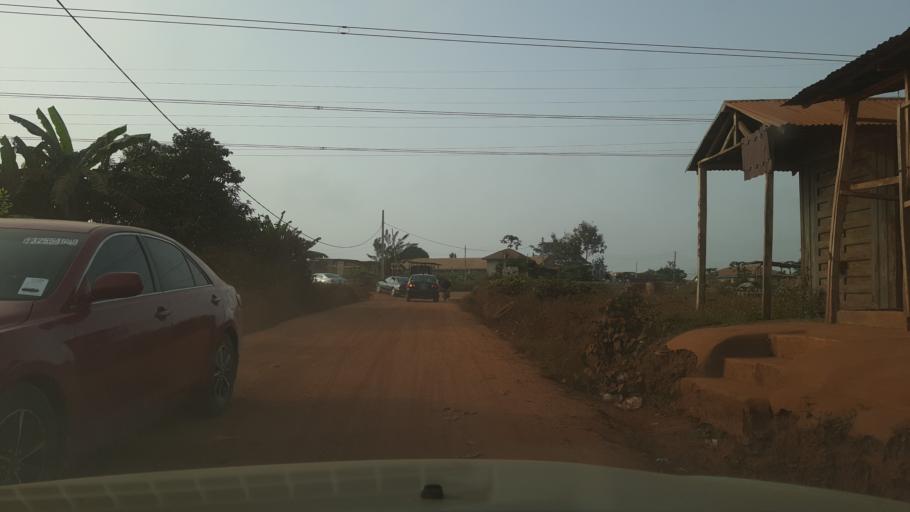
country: NG
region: Osun
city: Ilobu
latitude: 7.7935
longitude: 4.5010
